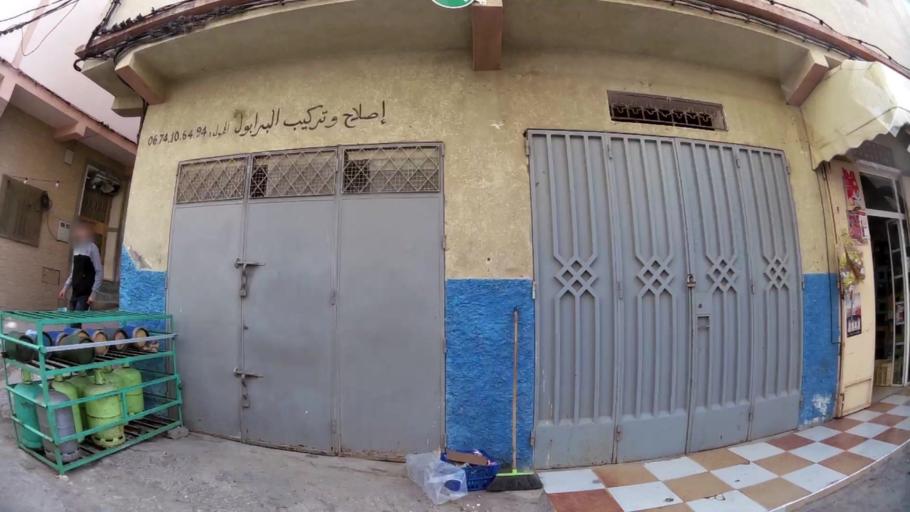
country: MA
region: Tanger-Tetouan
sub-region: Tanger-Assilah
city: Tangier
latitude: 35.7688
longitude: -5.7682
